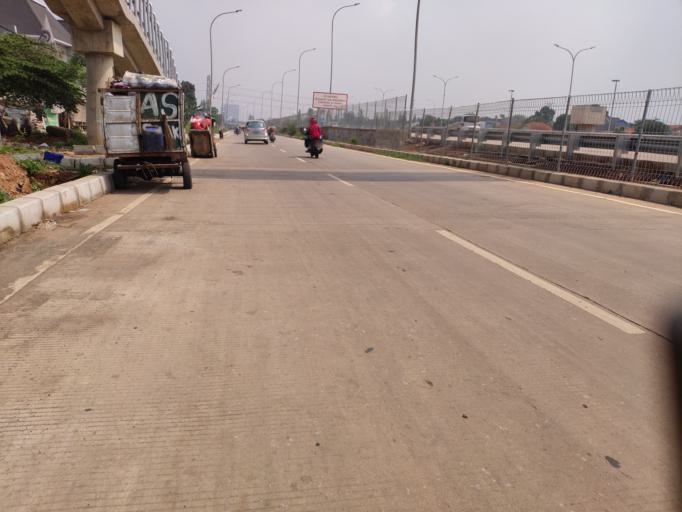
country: ID
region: West Java
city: Pamulang
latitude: -6.3212
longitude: 106.8031
